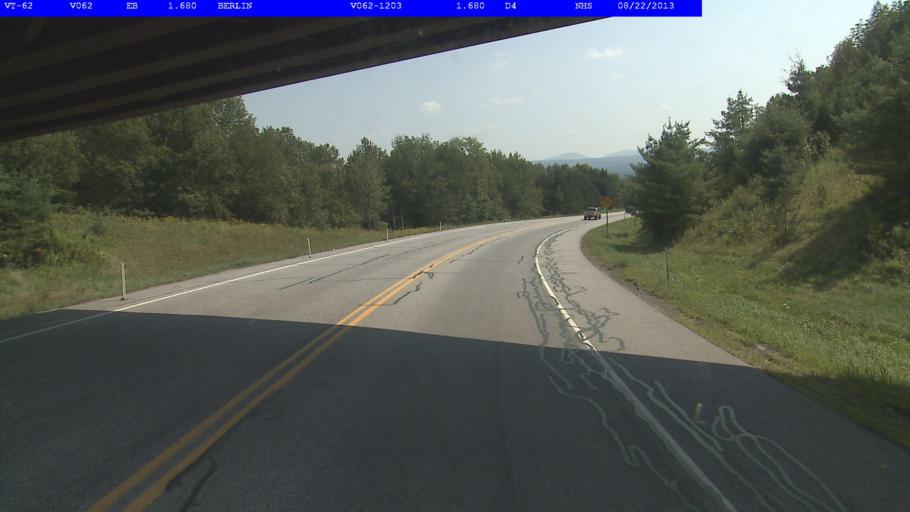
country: US
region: Vermont
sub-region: Washington County
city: Montpelier
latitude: 44.2214
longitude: -72.5560
